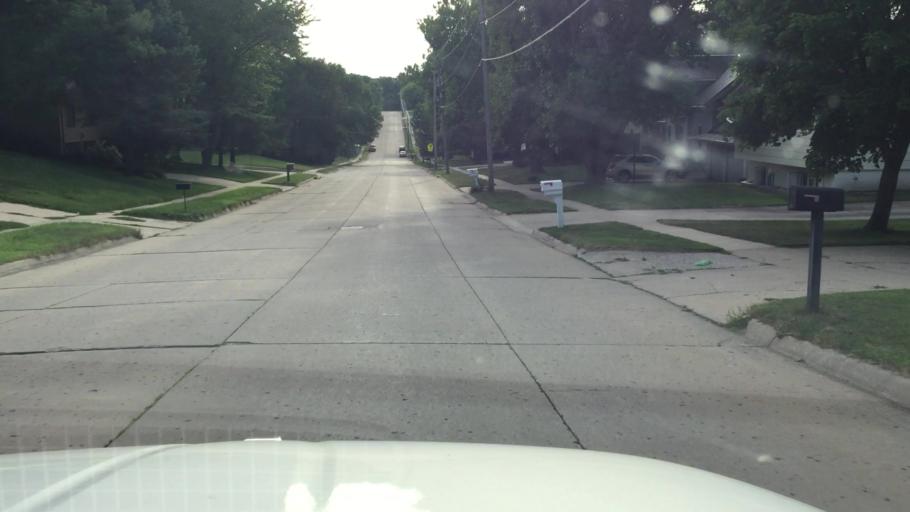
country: US
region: Iowa
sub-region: Johnson County
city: Iowa City
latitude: 41.6605
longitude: -91.4962
